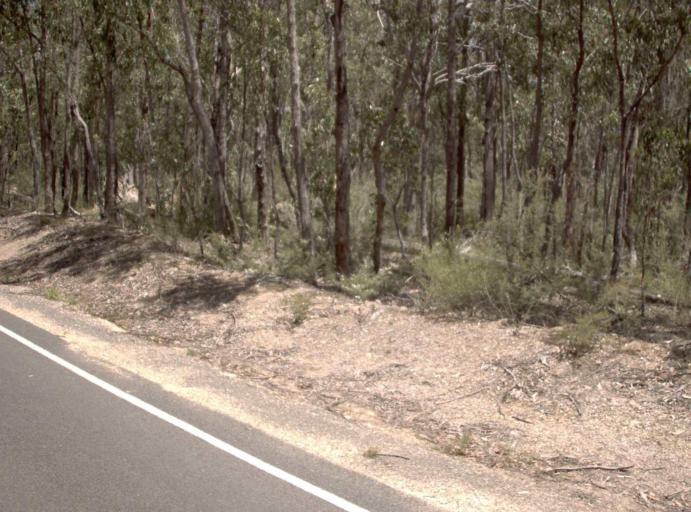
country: AU
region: Victoria
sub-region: East Gippsland
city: Lakes Entrance
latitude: -37.5912
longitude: 147.8928
